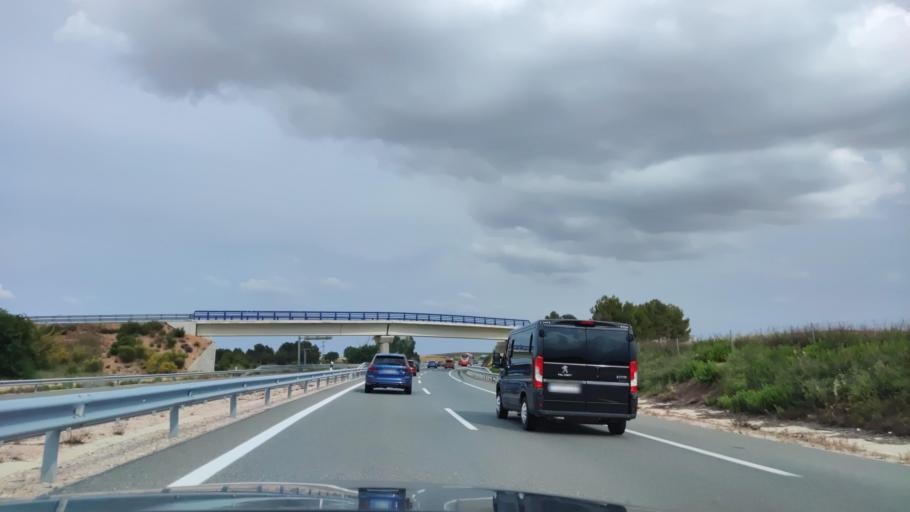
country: ES
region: Castille-La Mancha
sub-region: Provincia de Cuenca
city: Castillo de Garcimunoz
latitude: 39.6800
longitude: -2.3828
